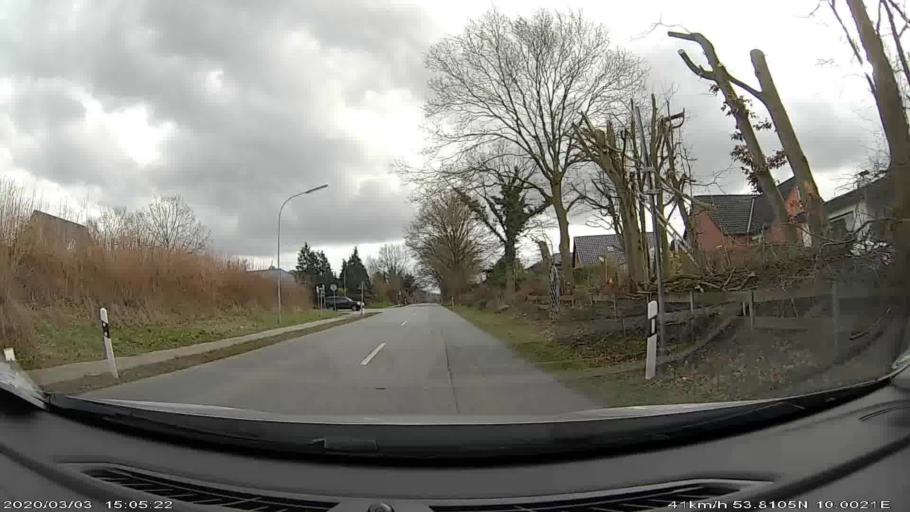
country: DE
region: Schleswig-Holstein
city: Kisdorf
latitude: 53.8107
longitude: 10.0020
